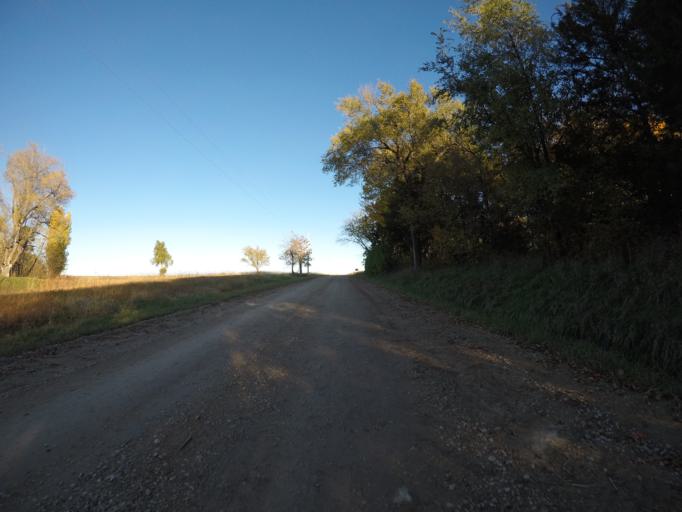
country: US
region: Kansas
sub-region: Riley County
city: Manhattan
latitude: 39.2691
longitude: -96.6964
